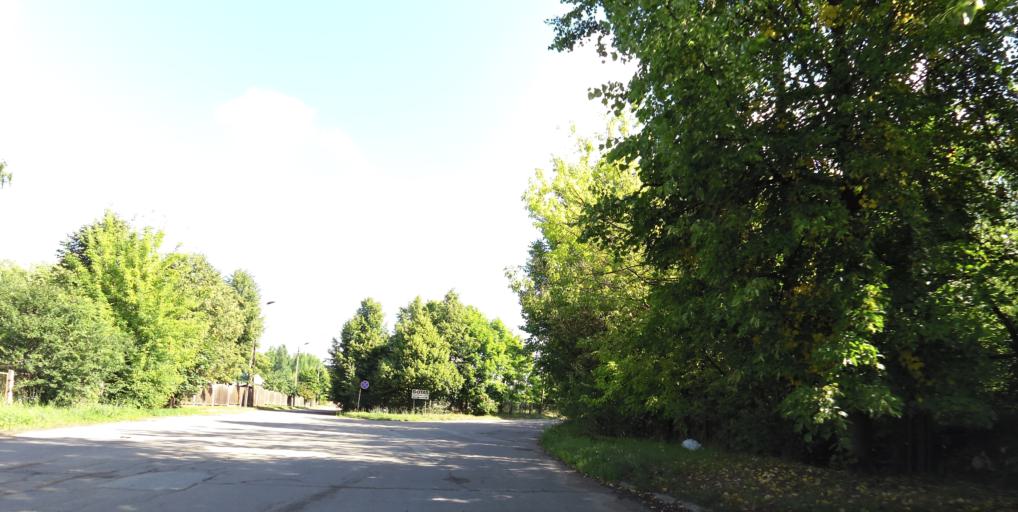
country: LT
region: Vilnius County
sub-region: Vilnius
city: Vilnius
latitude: 54.7088
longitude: 25.2721
